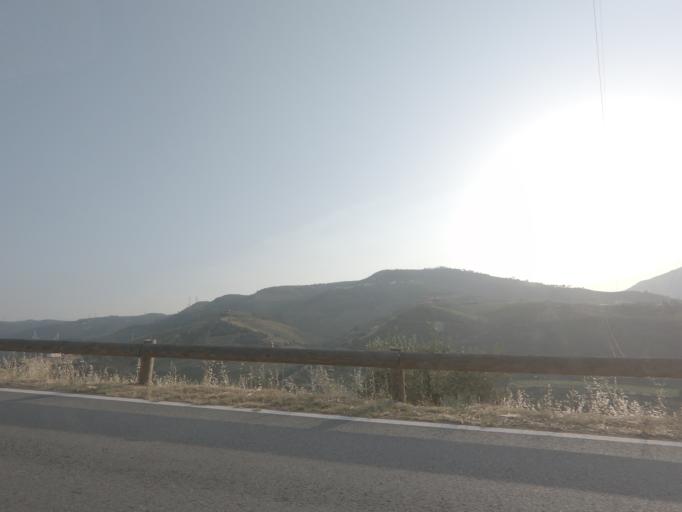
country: PT
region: Viseu
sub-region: Armamar
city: Armamar
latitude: 41.1555
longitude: -7.6383
